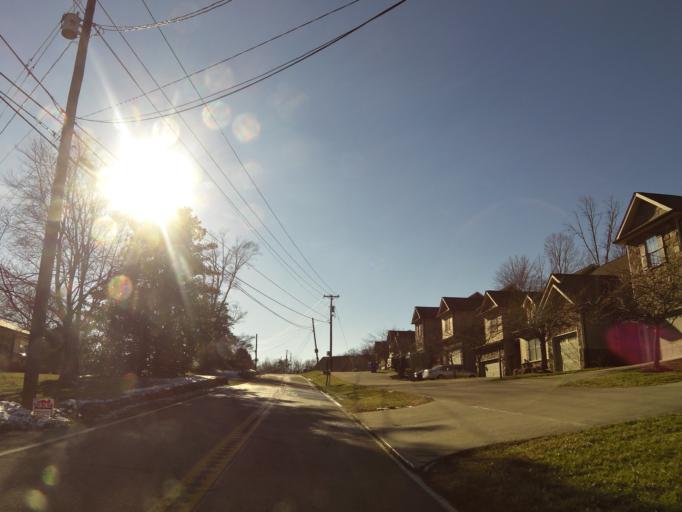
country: US
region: Tennessee
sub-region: Blount County
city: Louisville
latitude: 35.9031
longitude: -83.9992
